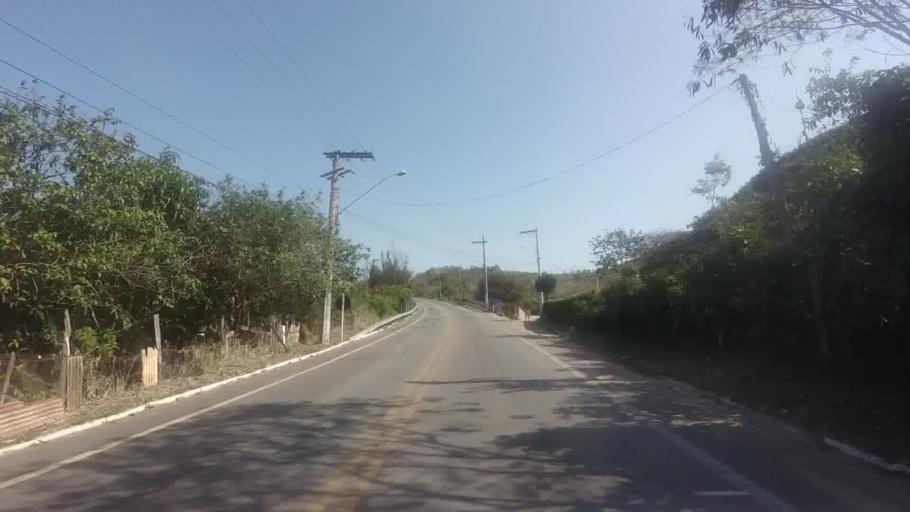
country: BR
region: Espirito Santo
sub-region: Piuma
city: Piuma
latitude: -20.8646
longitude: -40.7600
